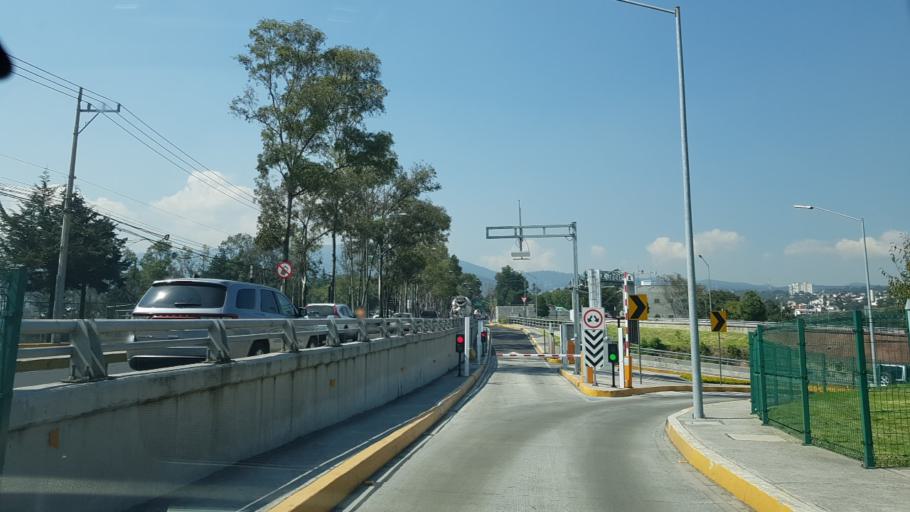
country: MX
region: Mexico City
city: Magdalena Contreras
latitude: 19.3452
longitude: -99.2390
